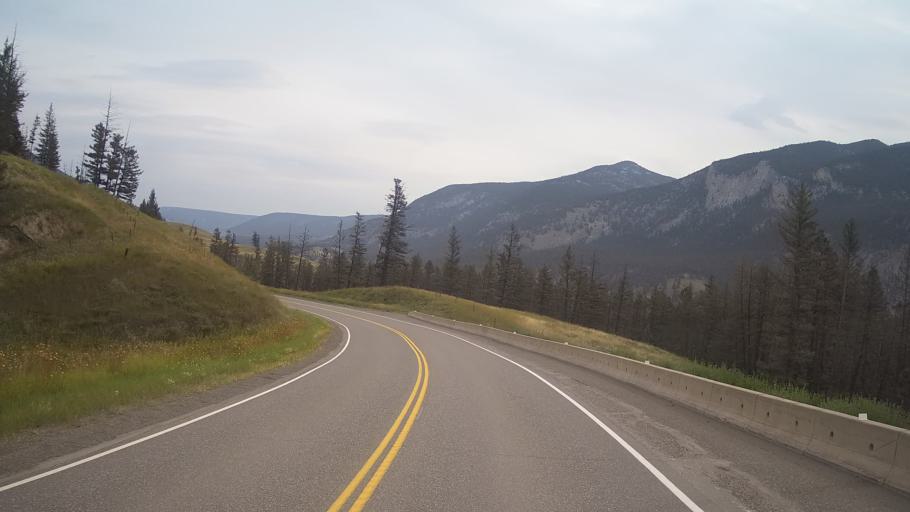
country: CA
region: British Columbia
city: Williams Lake
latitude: 51.9657
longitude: -122.2869
